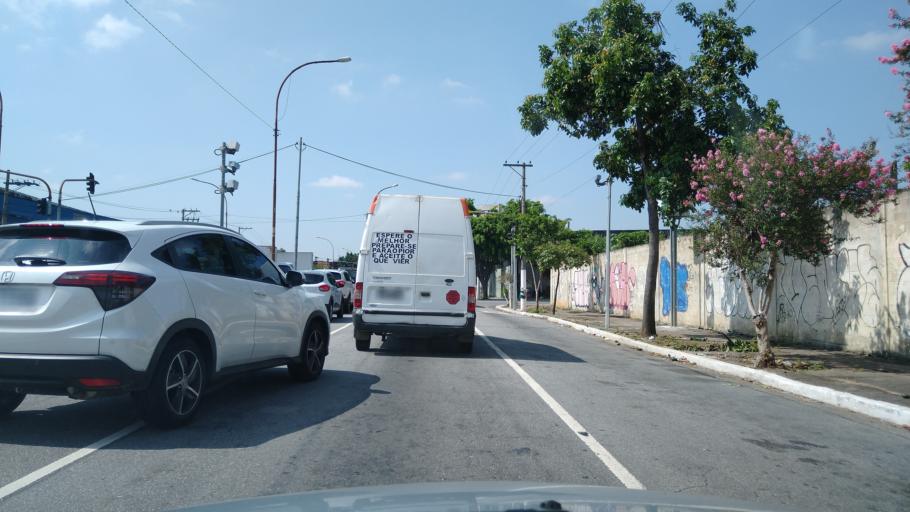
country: BR
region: Sao Paulo
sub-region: Sao Paulo
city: Sao Paulo
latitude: -23.5151
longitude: -46.5952
